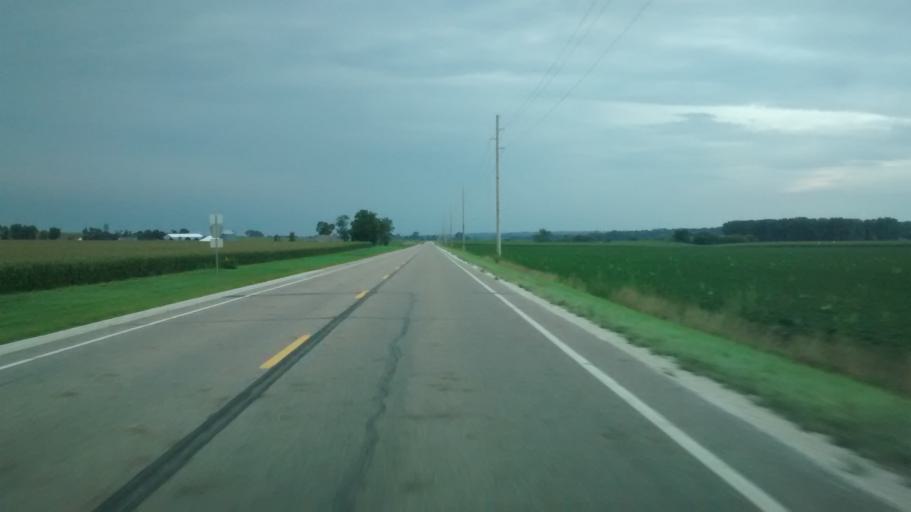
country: US
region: Iowa
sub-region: Plymouth County
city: Kingsley
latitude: 42.5747
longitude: -95.9931
